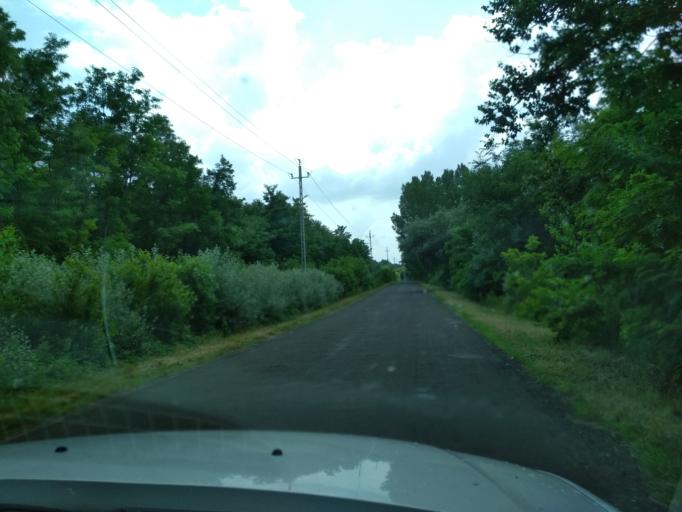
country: HU
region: Pest
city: Nagykata
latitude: 47.3863
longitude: 19.7560
